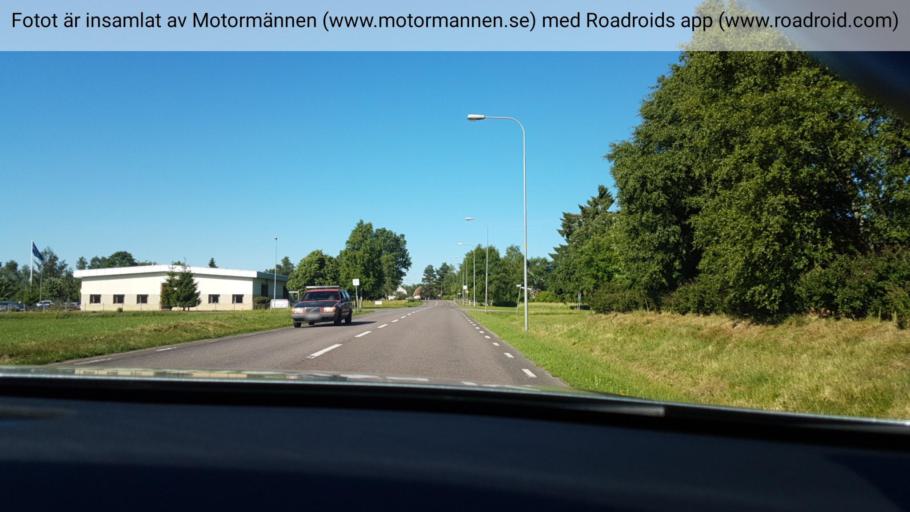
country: SE
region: Vaestra Goetaland
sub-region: Falkopings Kommun
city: Falkoeping
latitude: 58.0859
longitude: 13.5217
